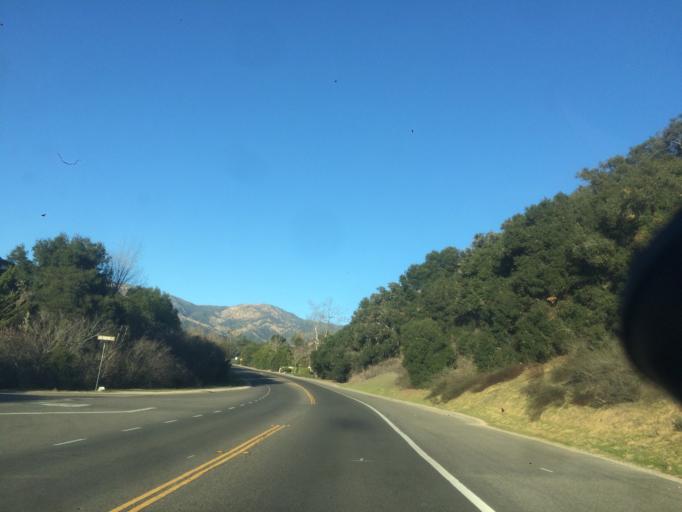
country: US
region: California
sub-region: Santa Barbara County
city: Mission Canyon
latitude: 34.4221
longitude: -119.7384
